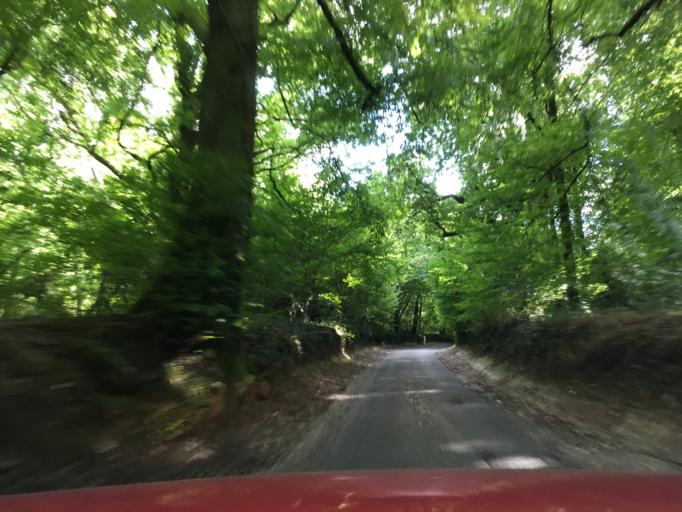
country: GB
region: England
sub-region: Hampshire
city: Chandlers Ford
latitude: 51.0664
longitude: -1.3791
